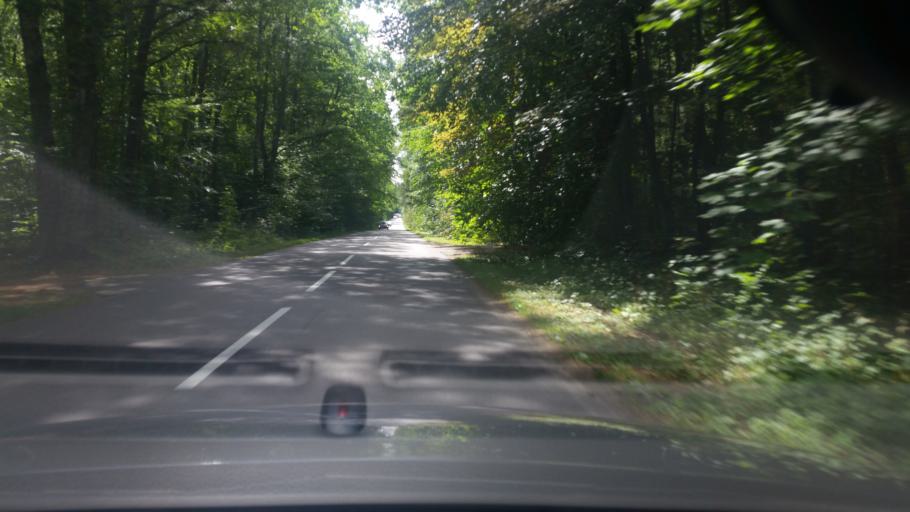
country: PL
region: Pomeranian Voivodeship
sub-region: Powiat wejherowski
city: Choczewo
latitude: 54.7545
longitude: 17.7477
